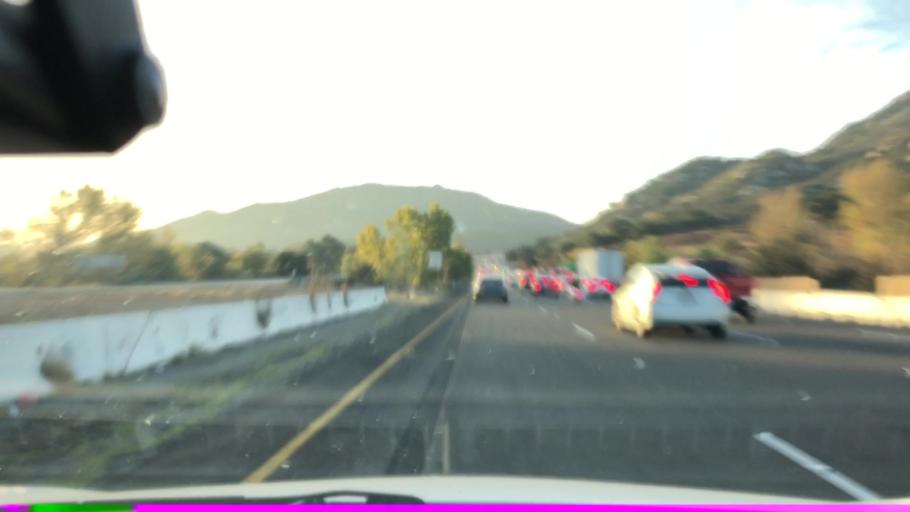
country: US
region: California
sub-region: Riverside County
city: Temecula
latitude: 33.4754
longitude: -117.1390
